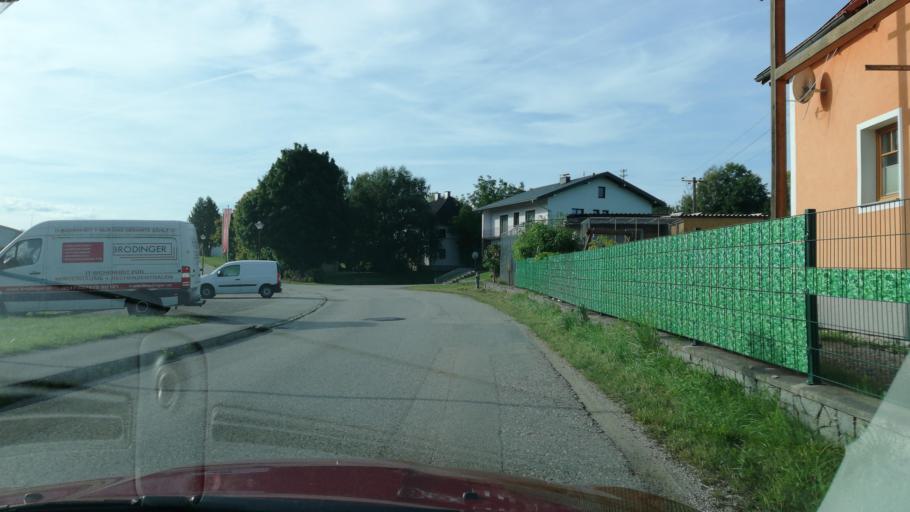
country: AT
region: Upper Austria
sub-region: Politischer Bezirk Vocklabruck
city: Redleiten
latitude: 48.0906
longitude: 13.5600
